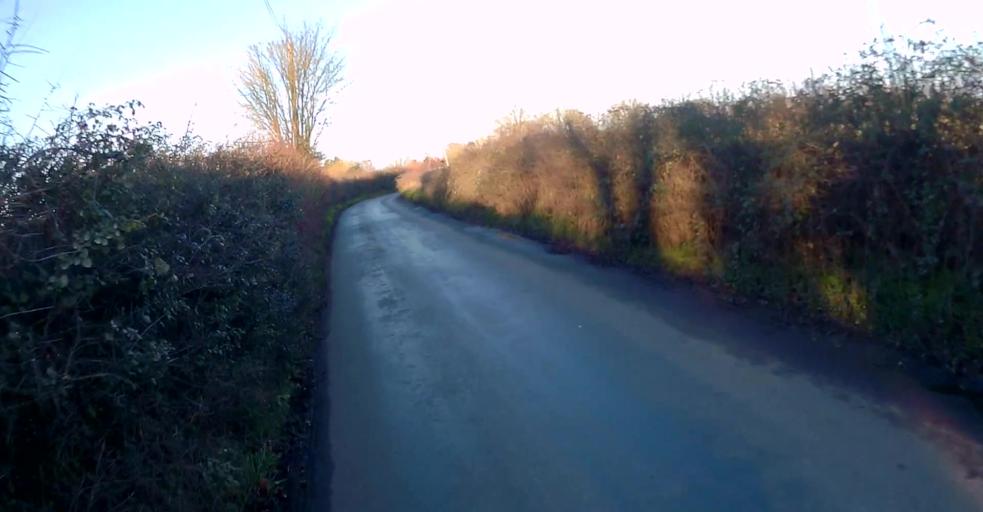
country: GB
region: England
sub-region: Hampshire
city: Hook
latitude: 51.3016
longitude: -0.9830
